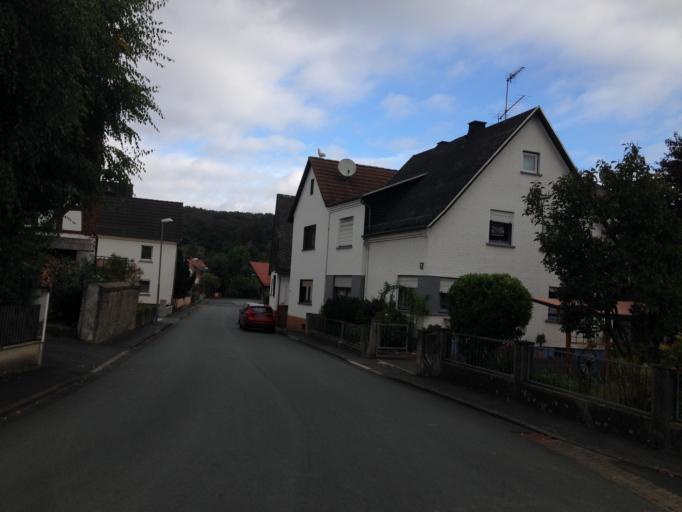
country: DE
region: Hesse
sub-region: Regierungsbezirk Giessen
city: Lohra
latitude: 50.6736
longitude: 8.5744
